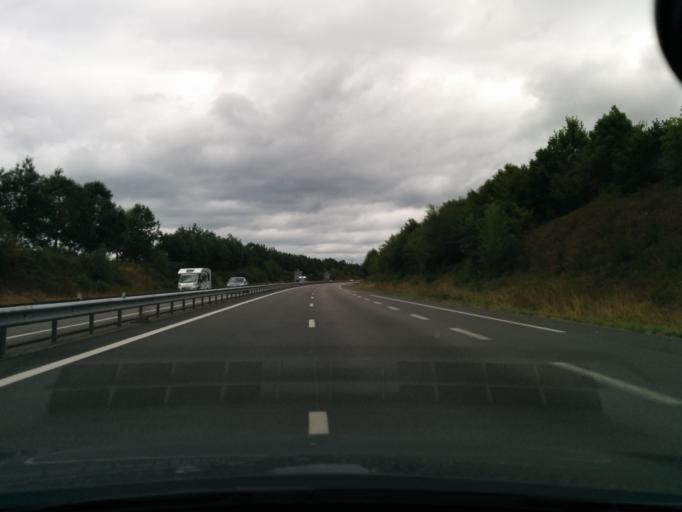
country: FR
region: Limousin
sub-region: Departement de la Haute-Vienne
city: Saint-Sulpice-les-Feuilles
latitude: 46.3184
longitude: 1.4177
